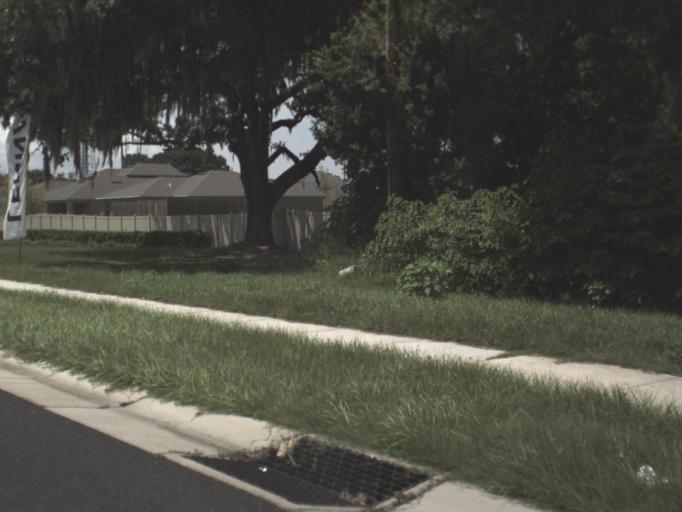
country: US
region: Florida
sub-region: Hillsborough County
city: Riverview
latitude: 27.8501
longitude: -82.3268
